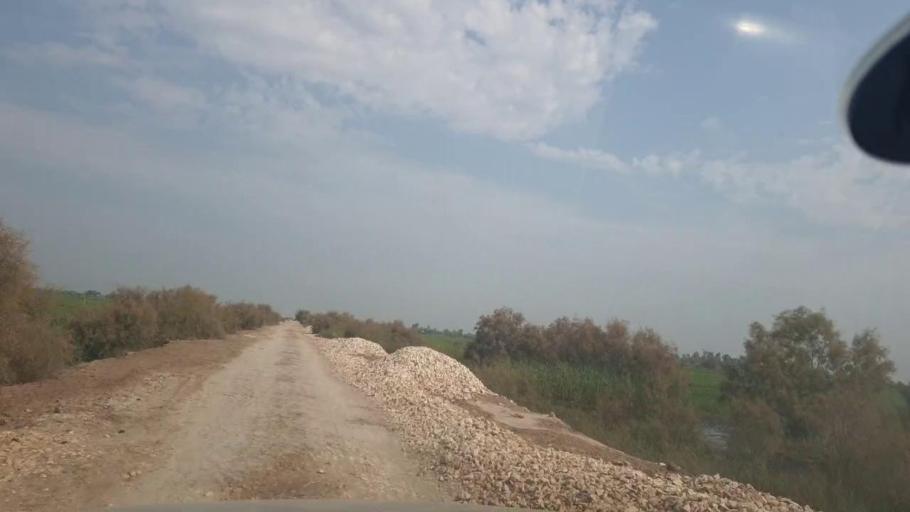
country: PK
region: Balochistan
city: Mehrabpur
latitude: 28.0954
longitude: 68.0937
